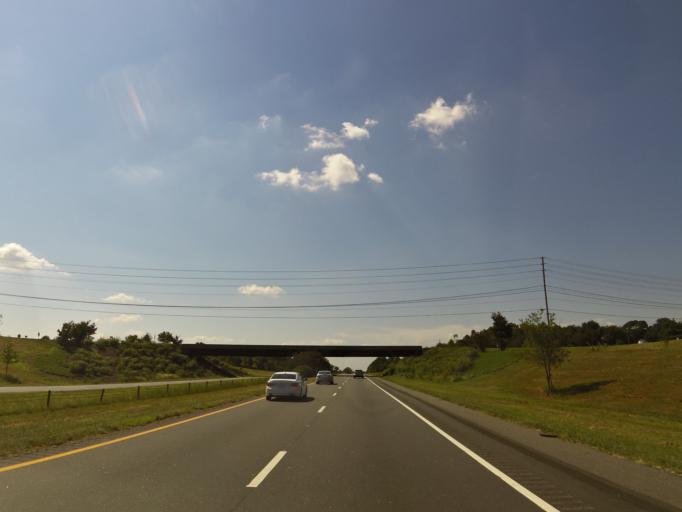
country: US
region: North Carolina
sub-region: Catawba County
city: Maiden
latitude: 35.5925
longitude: -81.2544
